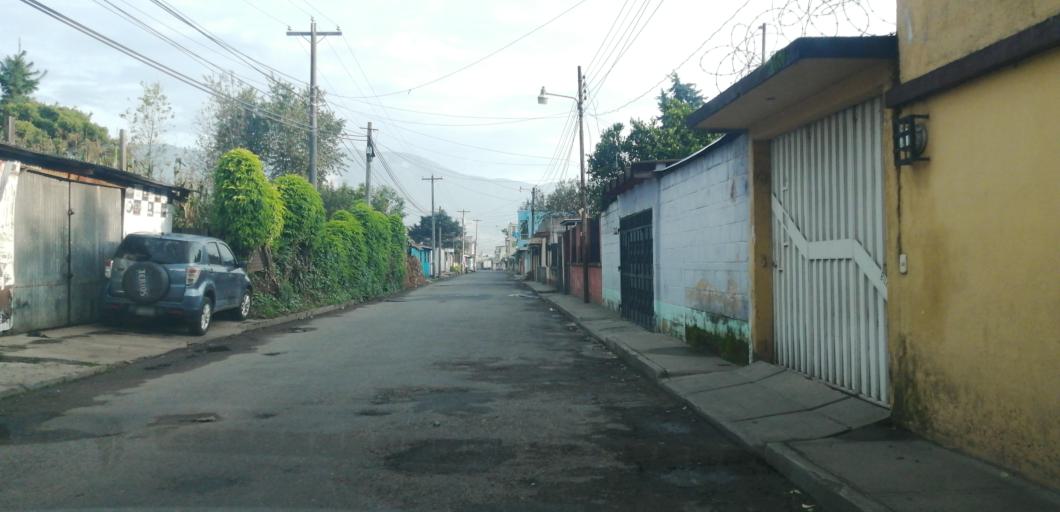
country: GT
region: Quetzaltenango
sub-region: Municipio de La Esperanza
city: La Esperanza
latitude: 14.8631
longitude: -91.5543
